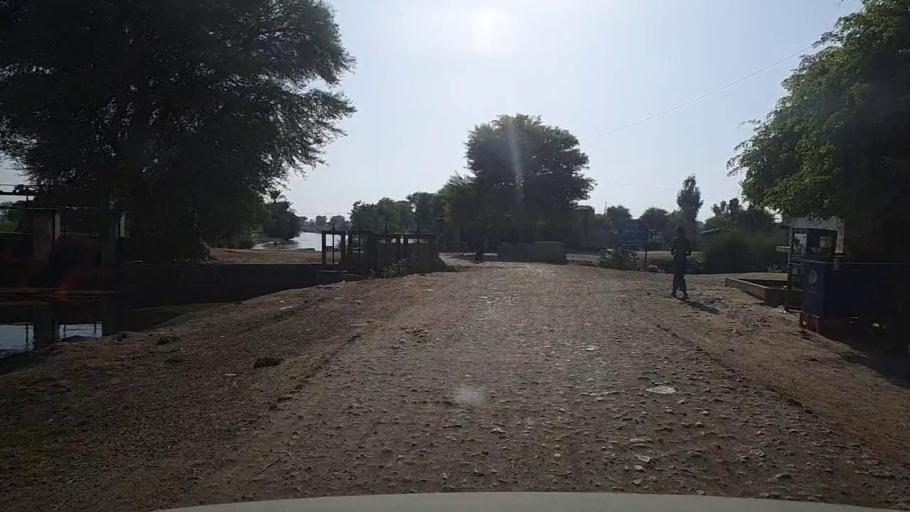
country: PK
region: Sindh
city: Kandhkot
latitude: 28.3510
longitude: 69.3641
